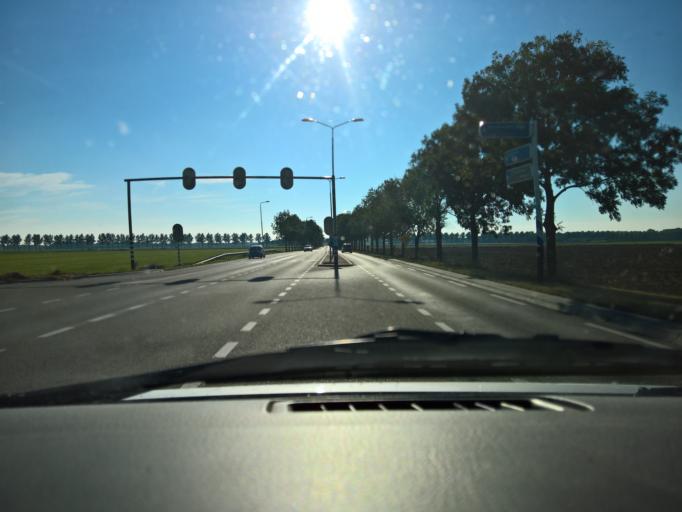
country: NL
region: Gelderland
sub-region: Gemeente Beuningen
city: Beuningen
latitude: 51.8465
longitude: 5.7448
